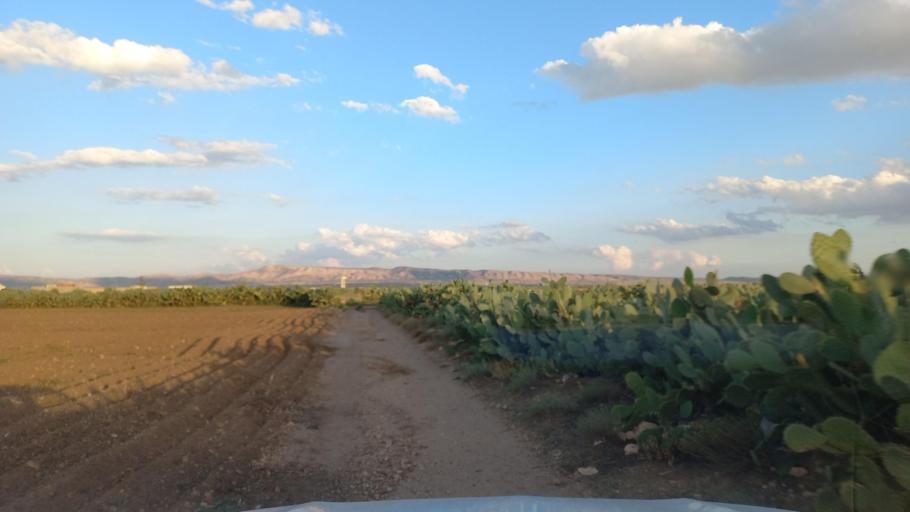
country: TN
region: Al Qasrayn
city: Sbiba
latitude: 35.3755
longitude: 9.0502
